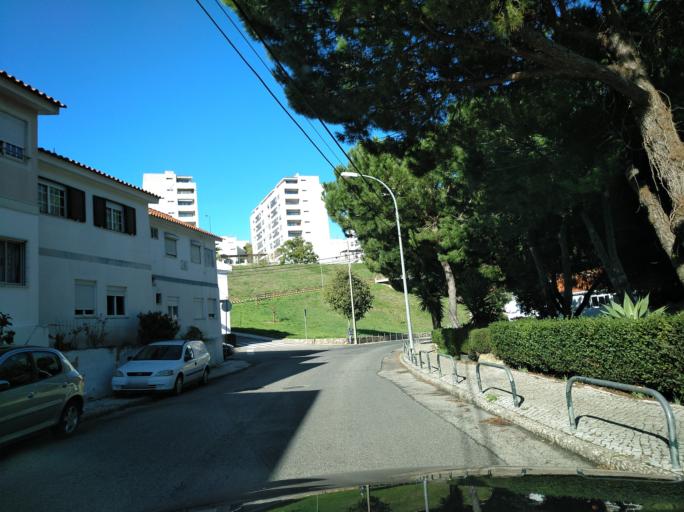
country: PT
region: Lisbon
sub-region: Loures
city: Moscavide
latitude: 38.7455
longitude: -9.1096
